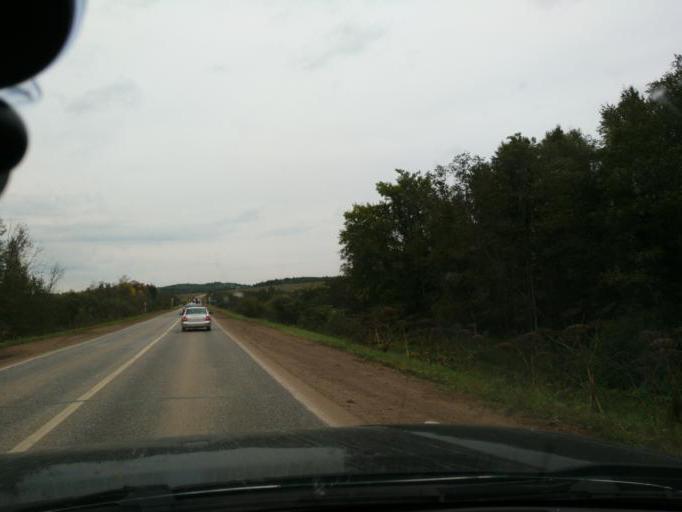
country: RU
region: Perm
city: Chernushka
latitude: 56.5583
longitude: 56.1131
